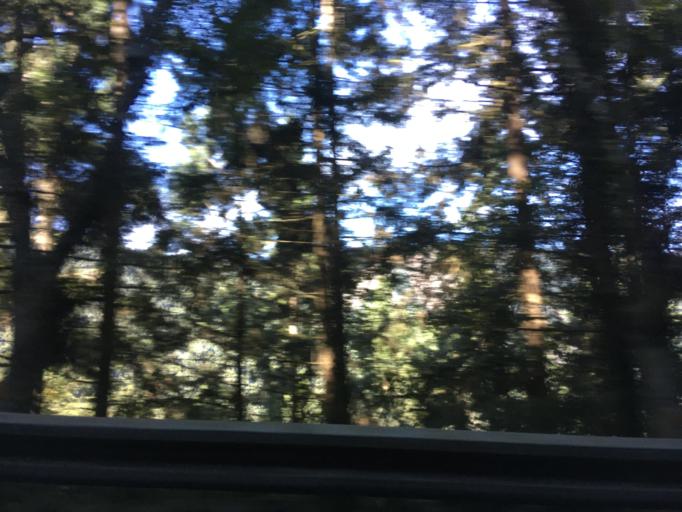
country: TW
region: Taiwan
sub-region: Yilan
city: Yilan
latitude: 24.5436
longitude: 121.5109
